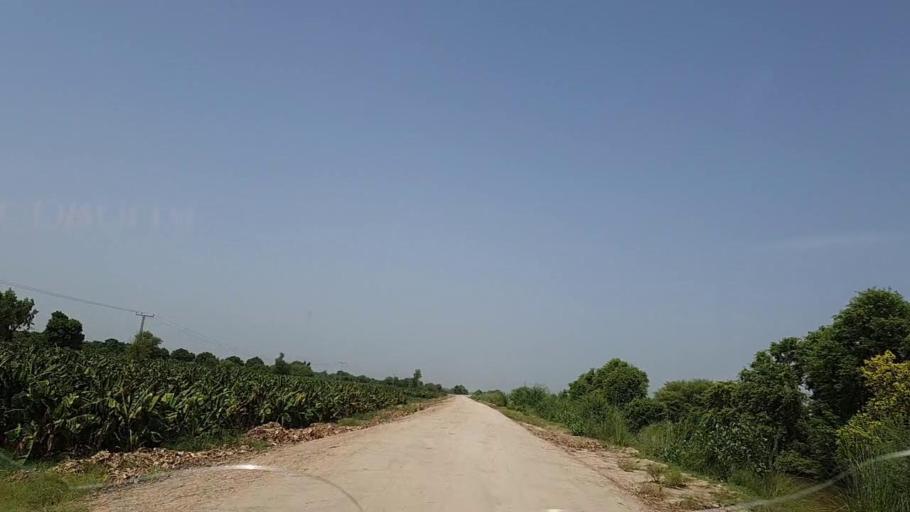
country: PK
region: Sindh
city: Kandiaro
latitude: 27.0308
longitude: 68.1458
